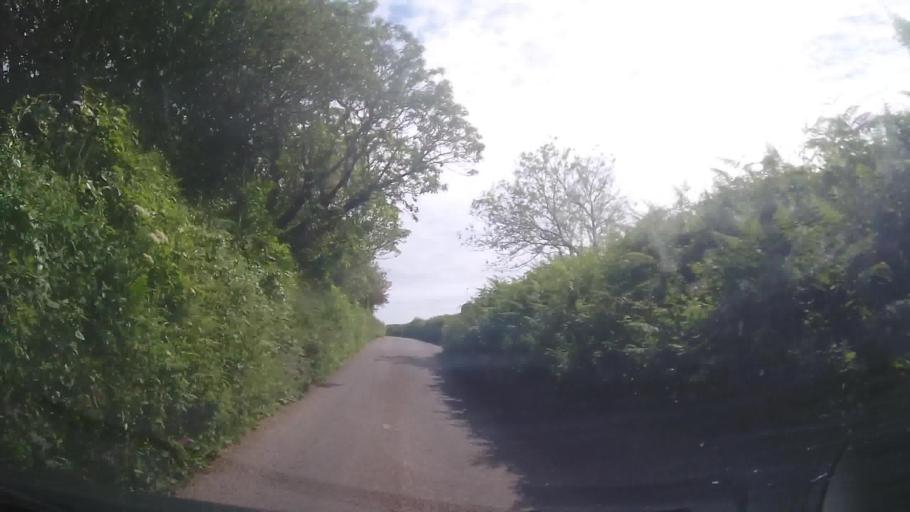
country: GB
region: England
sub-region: Devon
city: Salcombe
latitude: 50.2713
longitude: -3.6794
